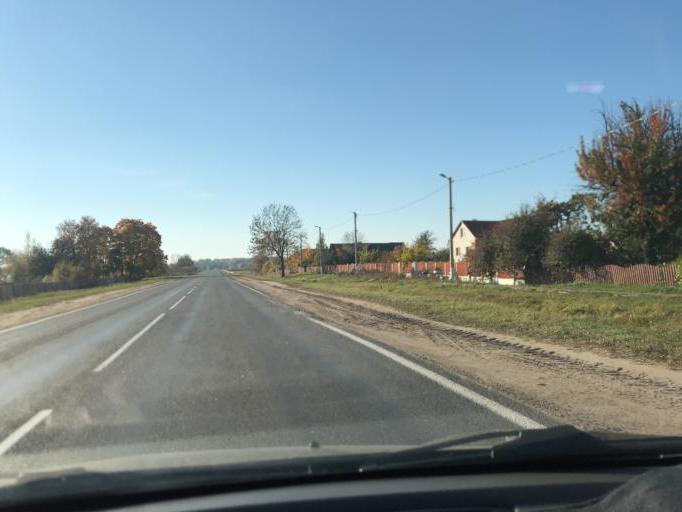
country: BY
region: Minsk
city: Staryya Darohi
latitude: 53.0541
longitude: 28.4119
